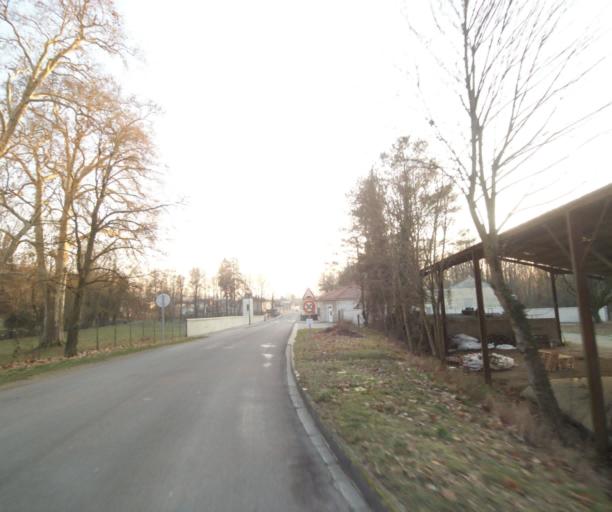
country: FR
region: Champagne-Ardenne
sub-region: Departement de la Haute-Marne
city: Bienville
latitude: 48.6109
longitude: 5.0467
